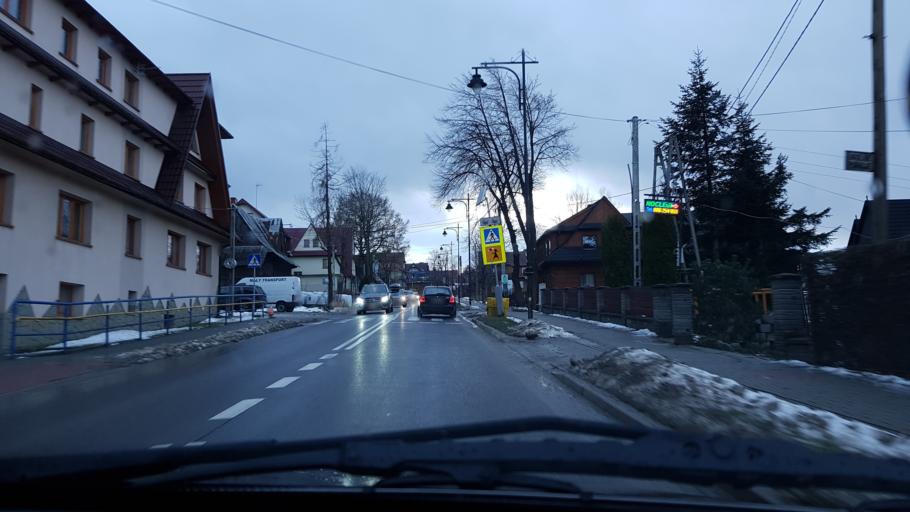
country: PL
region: Lesser Poland Voivodeship
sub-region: Powiat tatrzanski
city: Bukowina Tatrzanska
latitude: 49.3444
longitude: 20.1134
